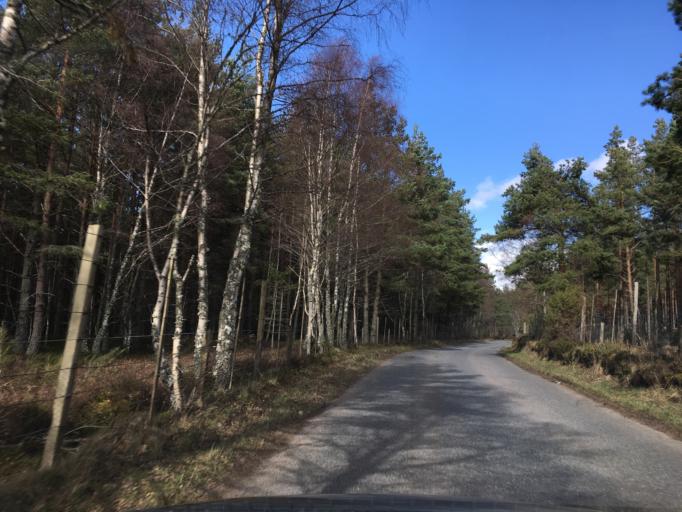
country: GB
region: Scotland
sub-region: Highland
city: Aviemore
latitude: 57.1953
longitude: -3.7992
